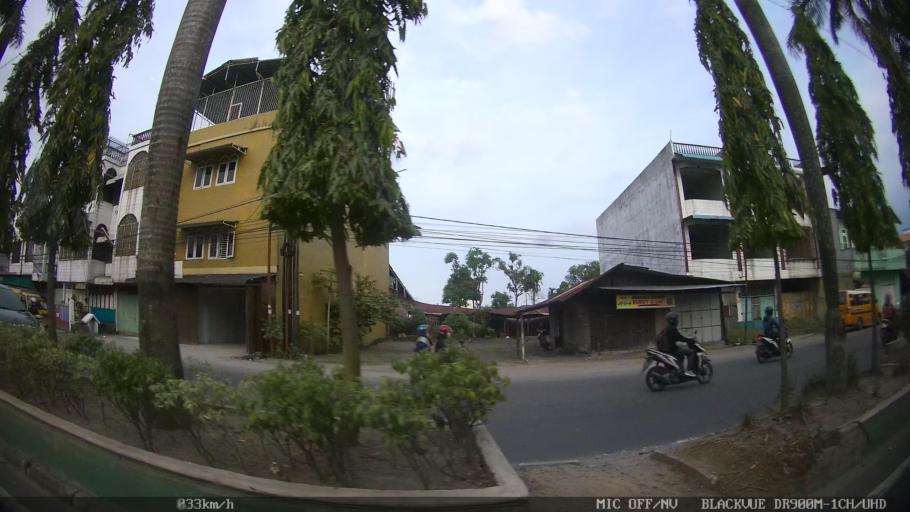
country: ID
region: North Sumatra
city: Sunggal
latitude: 3.5932
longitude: 98.6094
